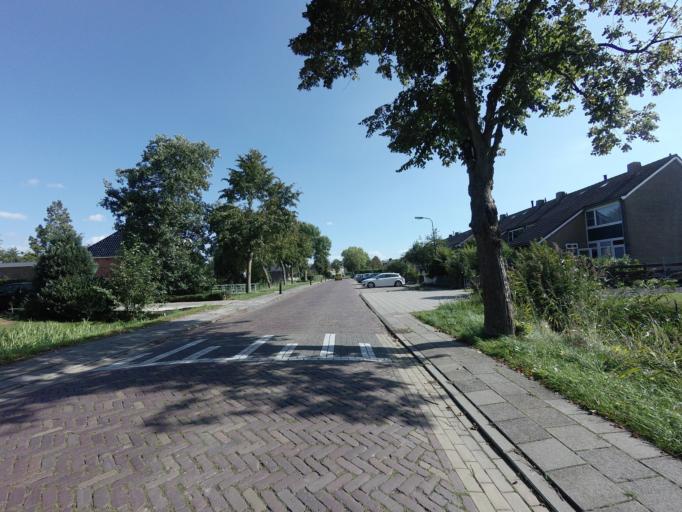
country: NL
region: Friesland
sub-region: Gemeente Littenseradiel
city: Makkum
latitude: 53.1007
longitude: 5.6445
